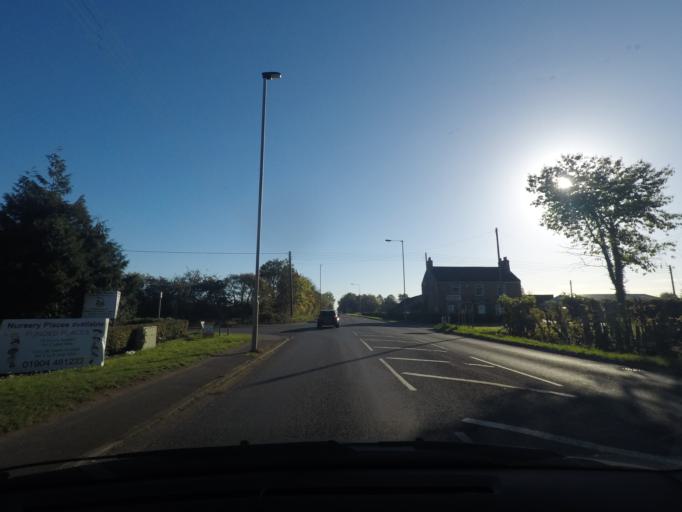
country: GB
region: England
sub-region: City of York
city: Holtby
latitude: 53.9548
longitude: -0.9722
